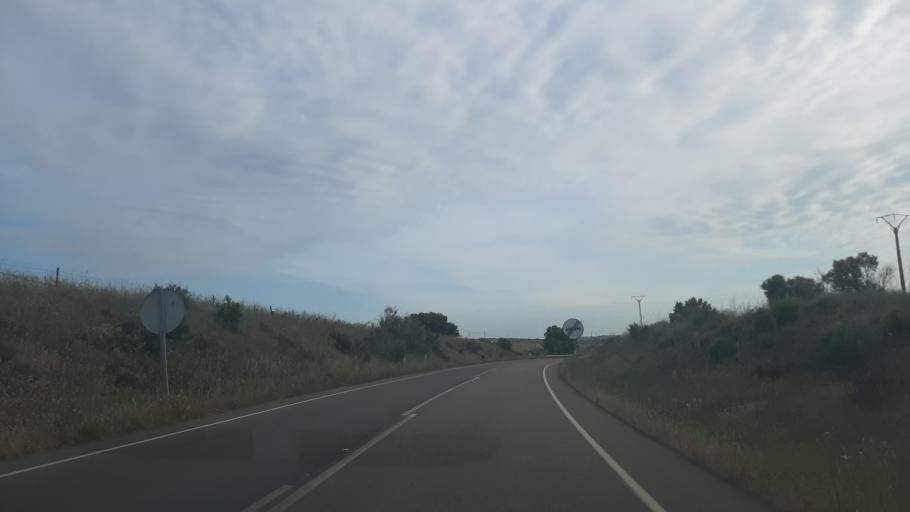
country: ES
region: Castille and Leon
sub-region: Provincia de Salamanca
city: Gallegos de Arganan
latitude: 40.6083
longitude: -6.7067
